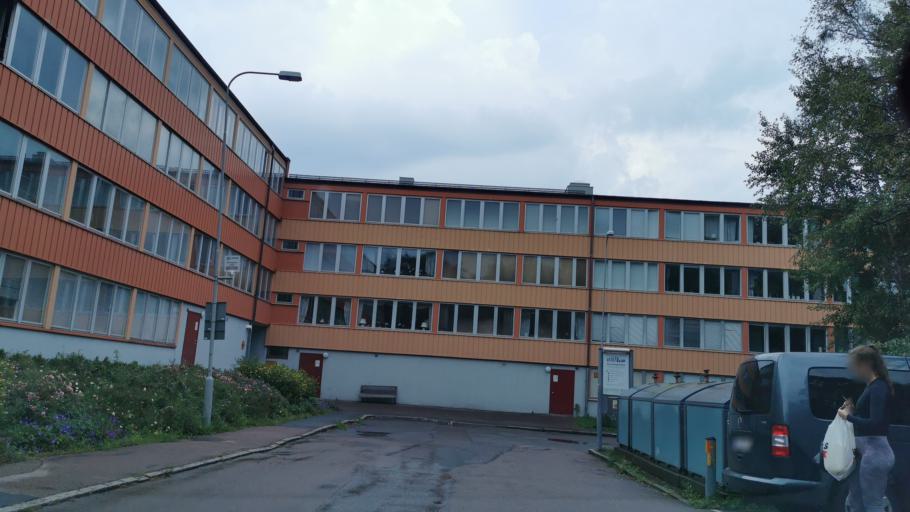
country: SE
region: Vaestra Goetaland
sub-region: Goteborg
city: Majorna
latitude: 57.6634
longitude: 11.9218
